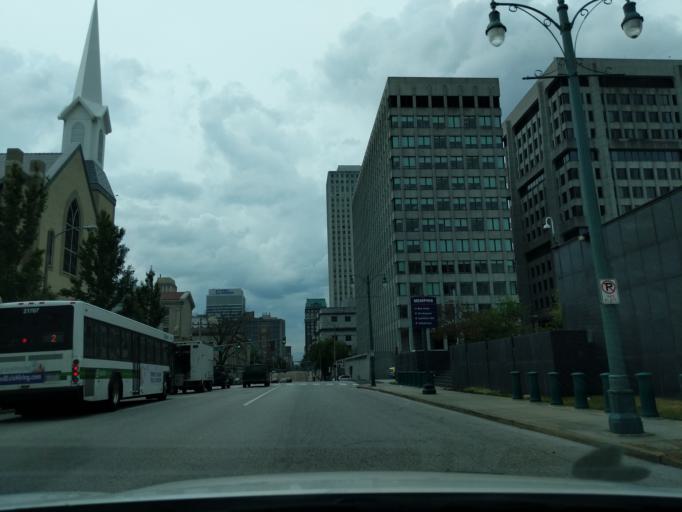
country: US
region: Tennessee
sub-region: Shelby County
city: Memphis
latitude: 35.1504
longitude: -90.0494
